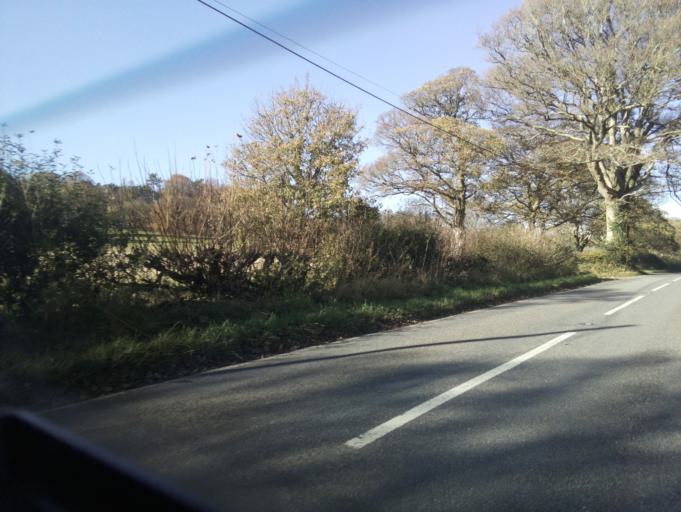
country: GB
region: England
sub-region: Dorset
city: Sherborne
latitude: 50.8319
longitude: -2.4830
